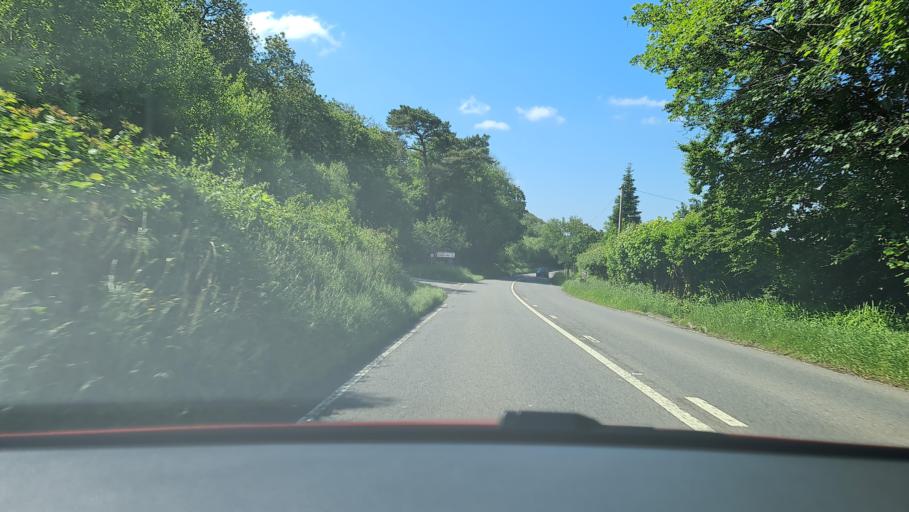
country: GB
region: England
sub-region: Cornwall
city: Lostwithiel
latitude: 50.4206
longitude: -4.6436
